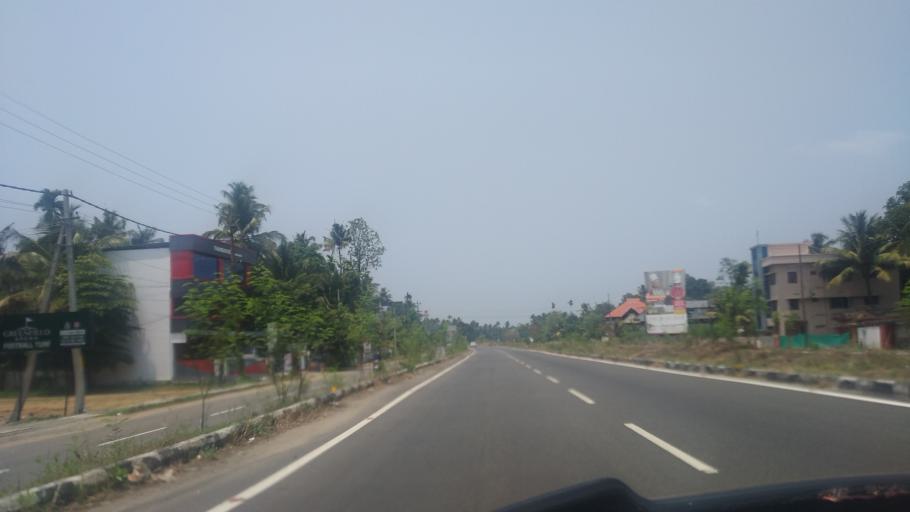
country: IN
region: Kerala
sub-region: Thrissur District
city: Kodungallur
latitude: 10.2145
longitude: 76.1975
